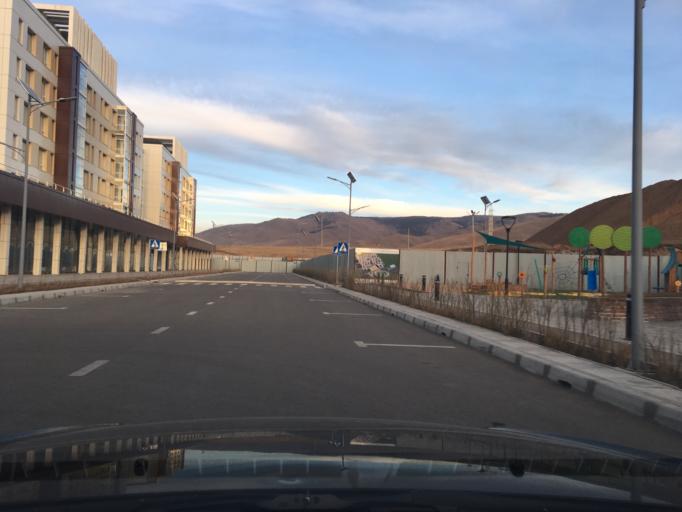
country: MN
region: Ulaanbaatar
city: Ulaanbaatar
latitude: 47.8485
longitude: 106.7932
